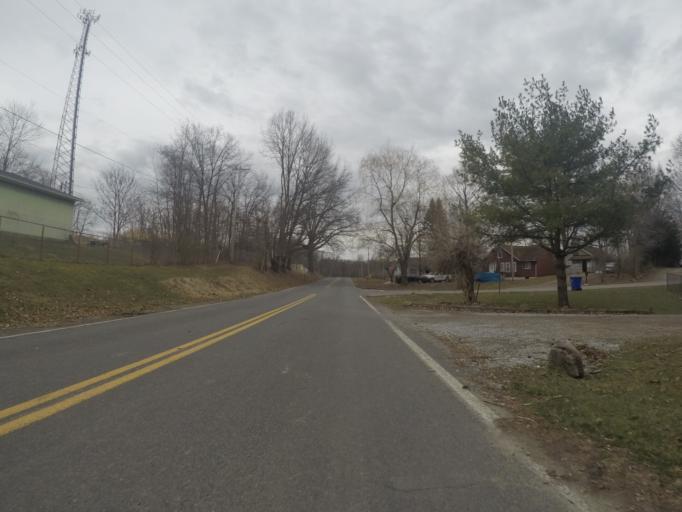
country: US
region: Ohio
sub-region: Portage County
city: Kent
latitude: 41.1706
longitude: -81.3111
